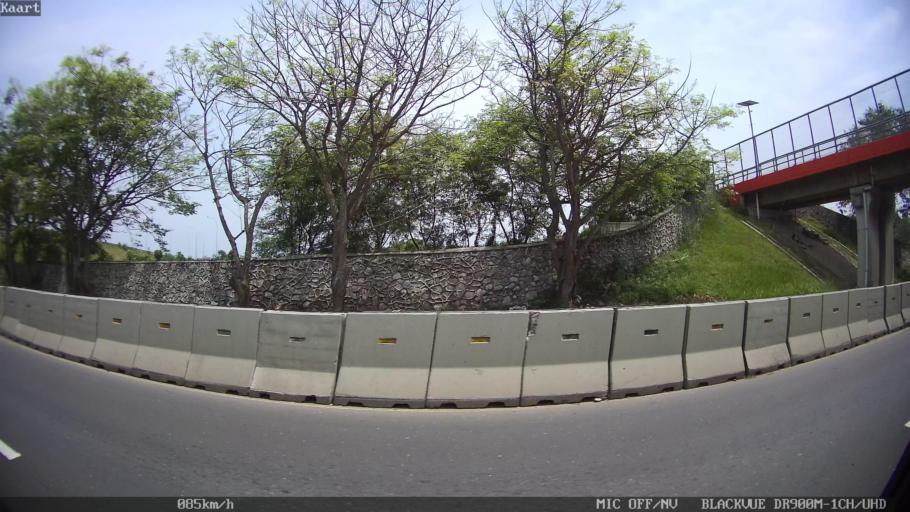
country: ID
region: Banten
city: Serang
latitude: -6.1387
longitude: 106.2435
